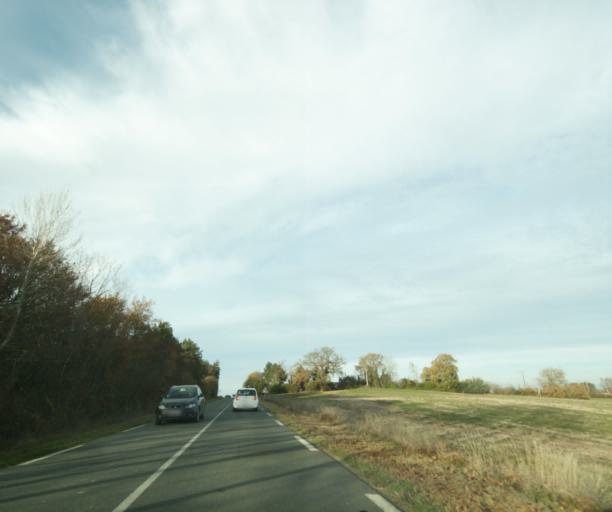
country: FR
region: Midi-Pyrenees
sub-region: Departement du Gers
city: Eauze
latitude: 43.8010
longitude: 0.0995
